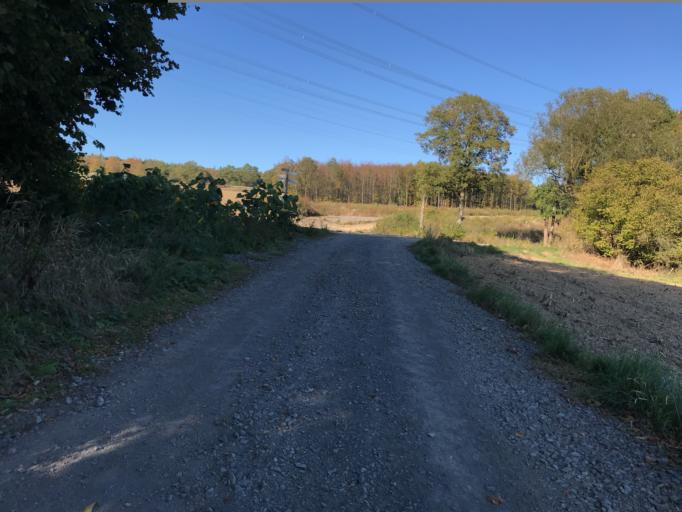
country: DE
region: Rheinland-Pfalz
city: Wolken
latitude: 50.3375
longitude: 7.4459
